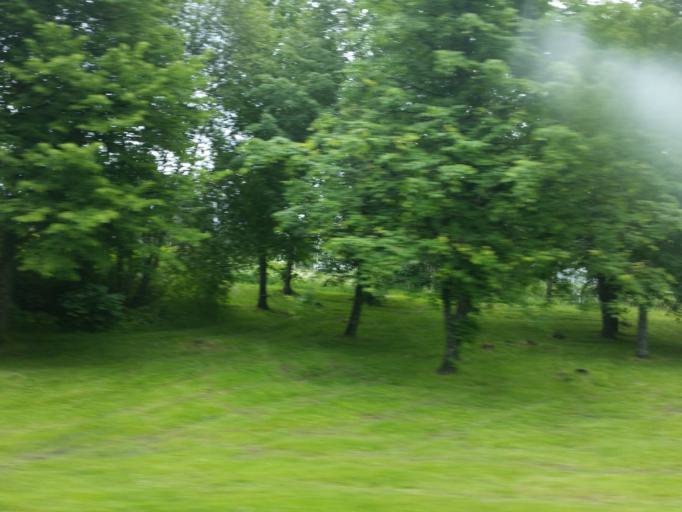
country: FI
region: Northern Savo
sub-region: Kuopio
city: Kuopio
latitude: 62.8933
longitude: 27.6406
